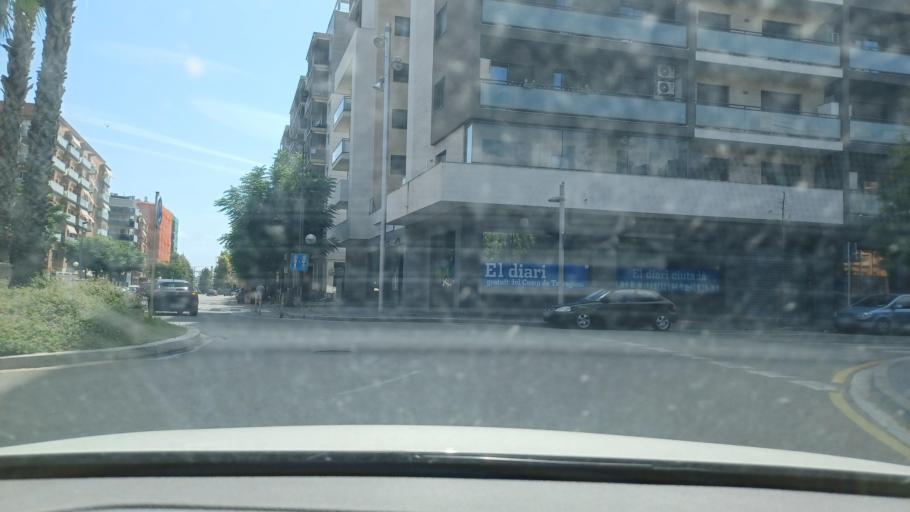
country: ES
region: Catalonia
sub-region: Provincia de Tarragona
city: Tarragona
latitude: 41.1138
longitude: 1.2411
